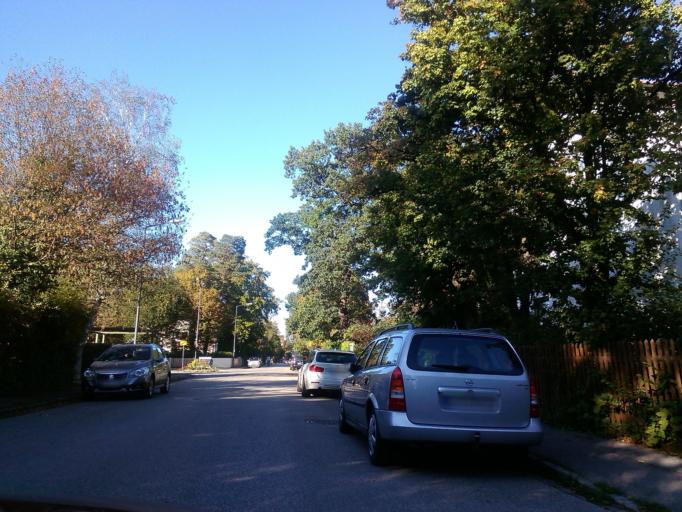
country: DE
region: Bavaria
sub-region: Upper Bavaria
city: Grafelfing
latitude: 48.1184
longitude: 11.4239
